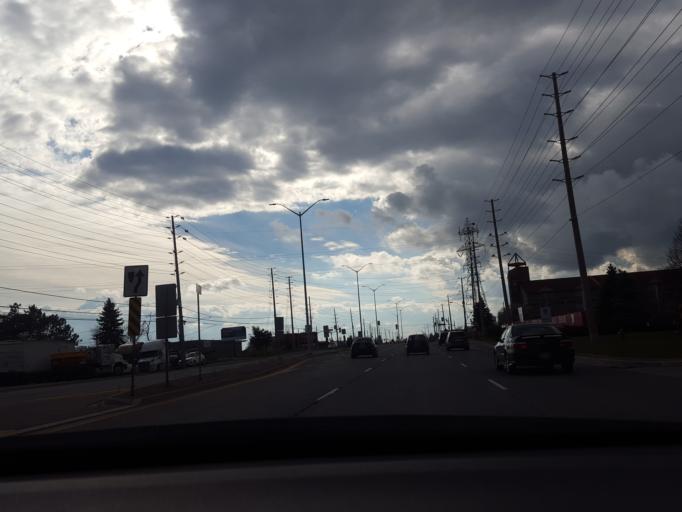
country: CA
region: Ontario
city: Brampton
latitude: 43.6501
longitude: -79.7017
